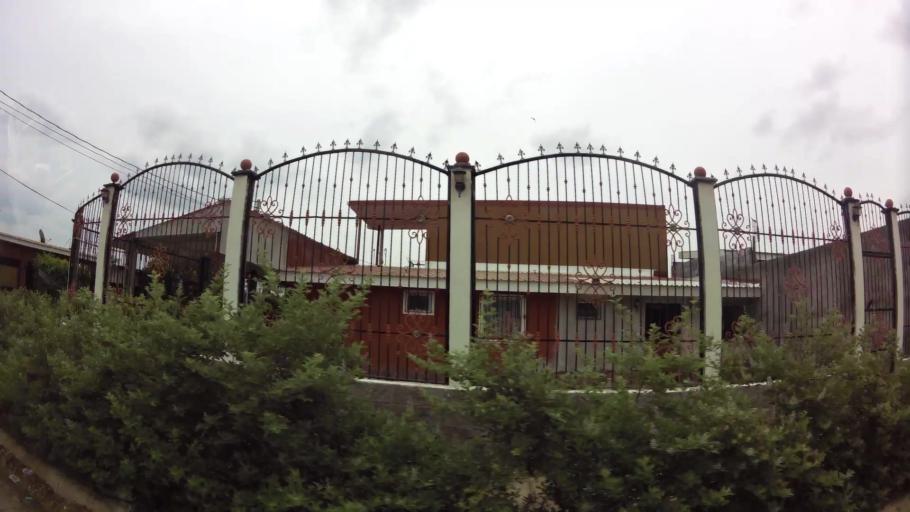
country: NI
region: Managua
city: Managua
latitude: 12.1217
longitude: -86.1827
